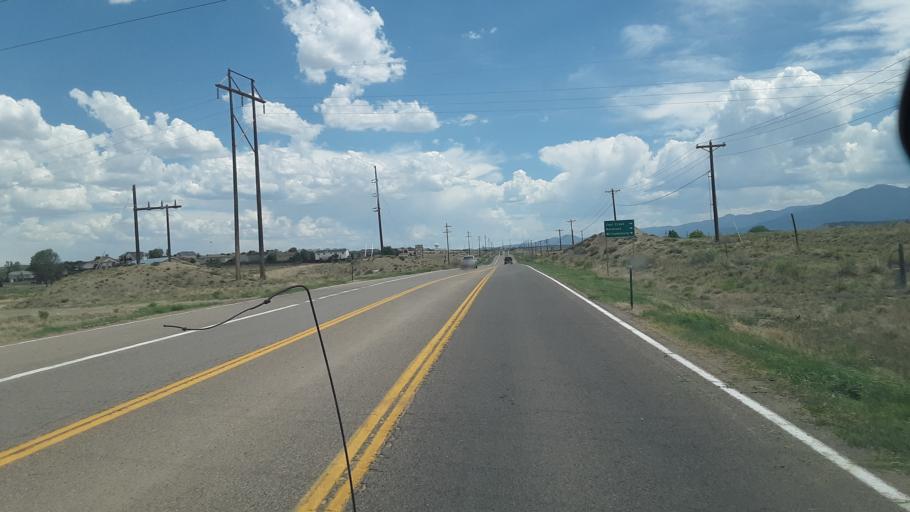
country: US
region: Colorado
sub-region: Fremont County
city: Florence
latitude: 38.3776
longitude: -105.1109
